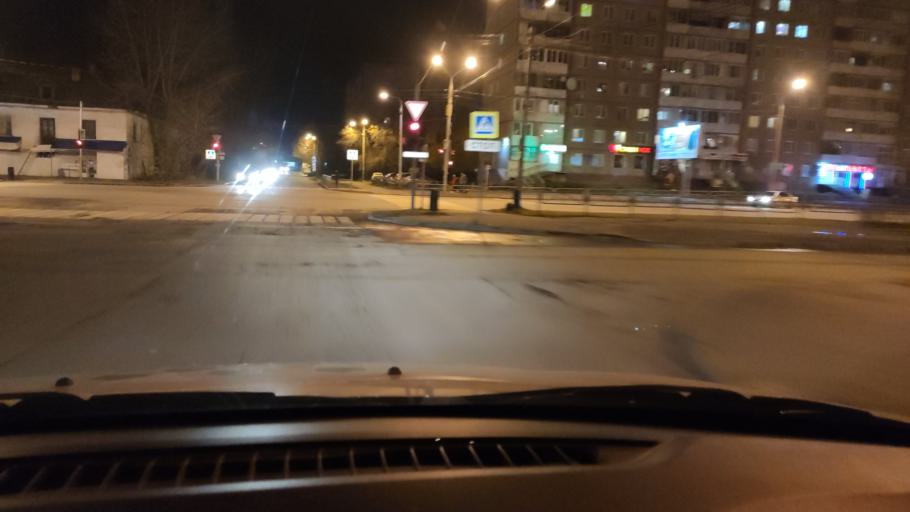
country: RU
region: Perm
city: Kondratovo
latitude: 57.9974
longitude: 56.1474
